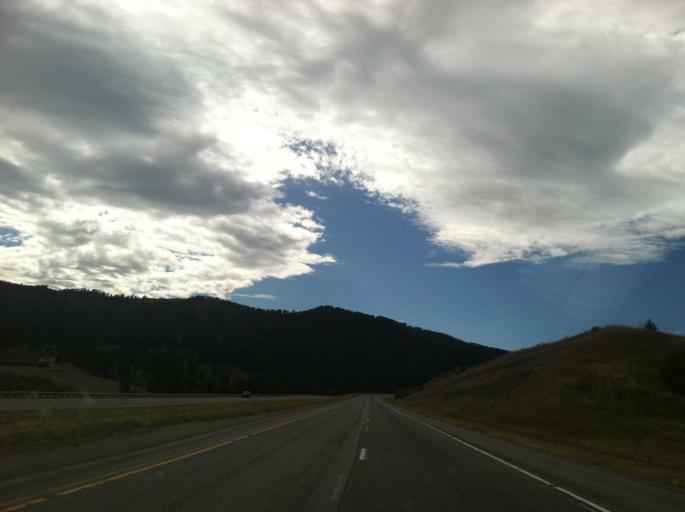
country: US
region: Montana
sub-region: Park County
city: Livingston
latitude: 45.6574
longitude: -110.7685
